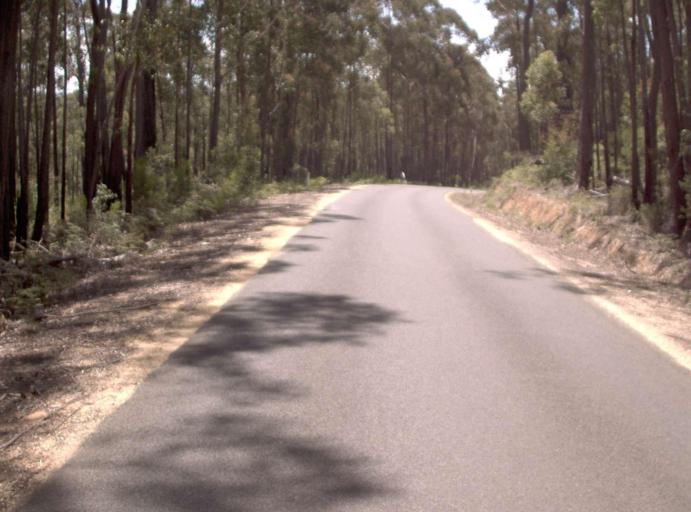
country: AU
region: New South Wales
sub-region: Bombala
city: Bombala
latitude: -37.5659
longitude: 148.9449
